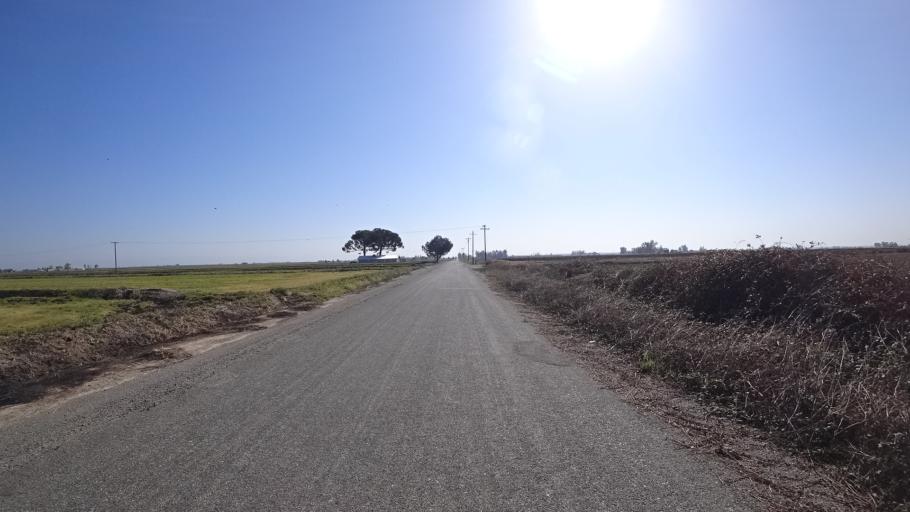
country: US
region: California
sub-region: Glenn County
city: Willows
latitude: 39.6017
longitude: -122.0757
